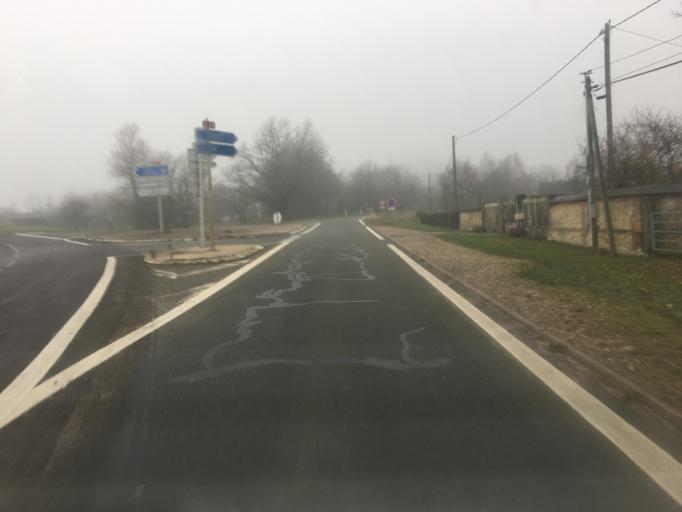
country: FR
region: Haute-Normandie
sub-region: Departement de la Seine-Maritime
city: Neufchatel-en-Bray
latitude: 49.7215
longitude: 1.4250
